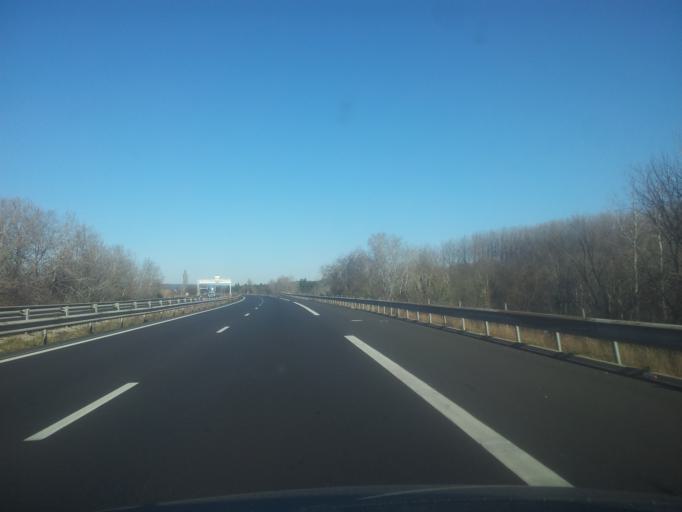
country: FR
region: Provence-Alpes-Cote d'Azur
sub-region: Departement du Vaucluse
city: Caderousse
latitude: 44.0953
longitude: 4.7874
